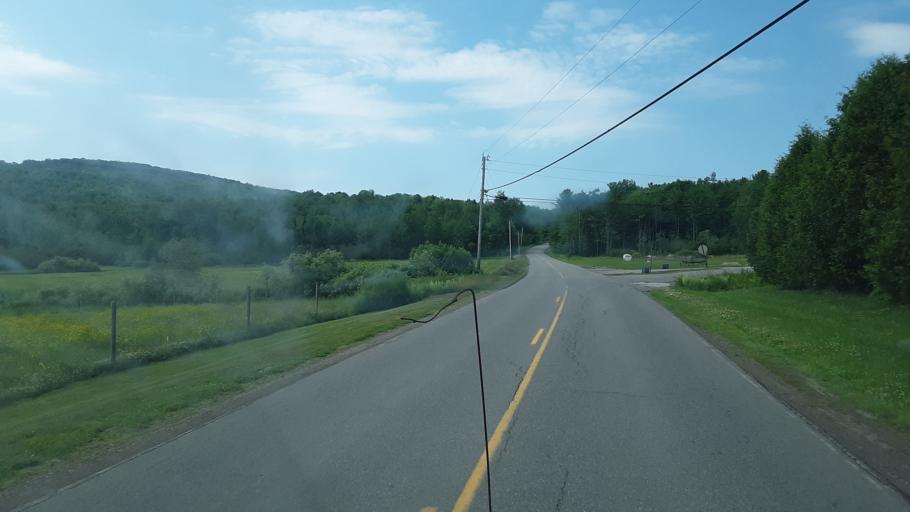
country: US
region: Maine
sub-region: Waldo County
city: Frankfort
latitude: 44.6000
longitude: -68.9403
